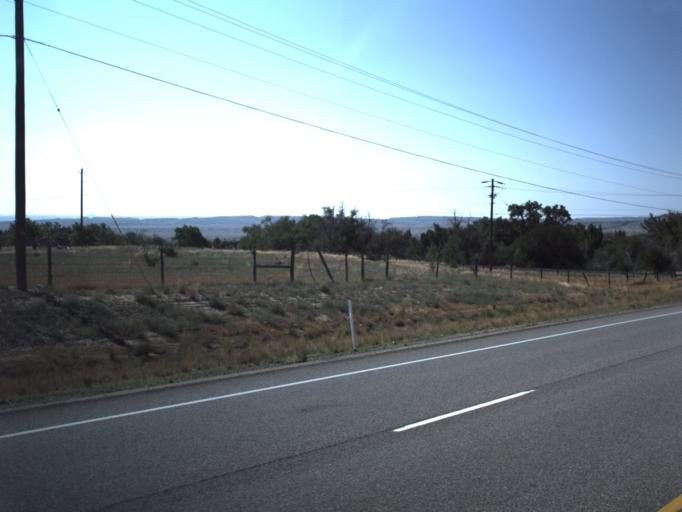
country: US
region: Utah
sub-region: Emery County
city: Ferron
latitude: 39.1000
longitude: -111.1317
